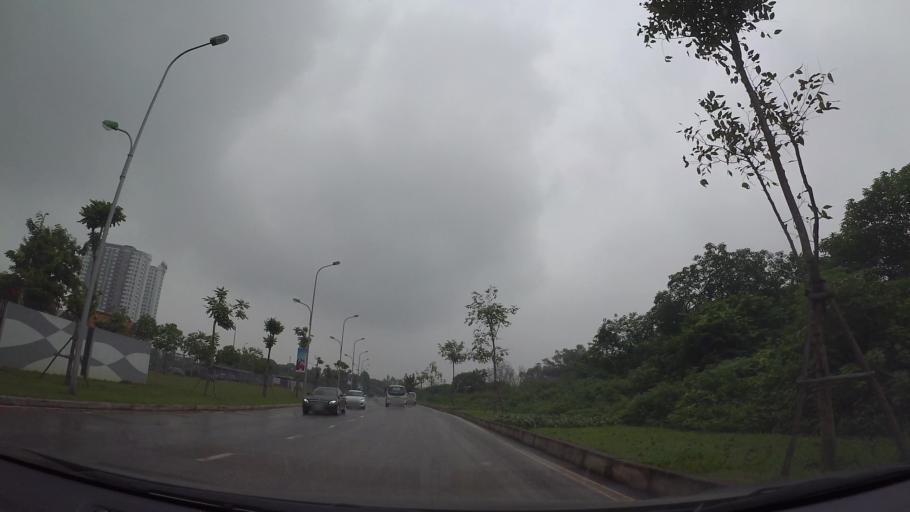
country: VN
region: Ha Noi
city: Van Dien
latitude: 20.9700
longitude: 105.8736
